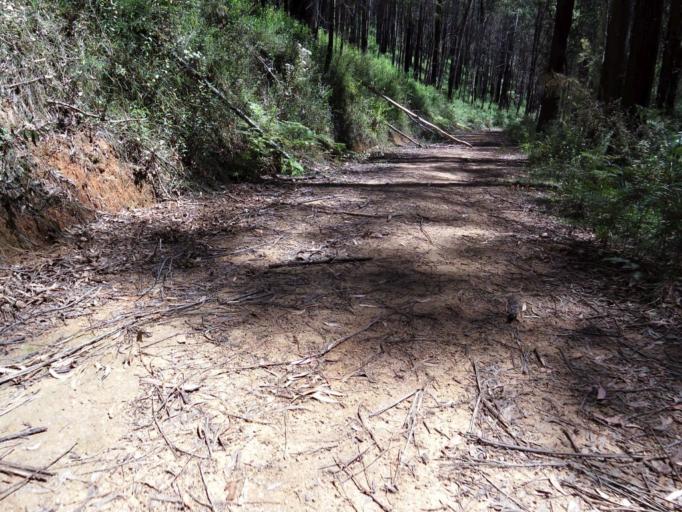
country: AU
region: Victoria
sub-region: Yarra Ranges
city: Millgrove
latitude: -37.8557
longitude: 145.7575
